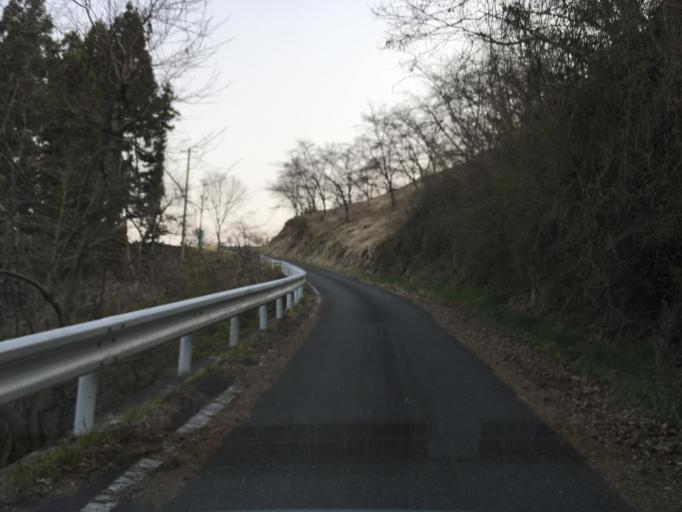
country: JP
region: Iwate
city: Ichinoseki
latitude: 38.9411
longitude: 141.2331
